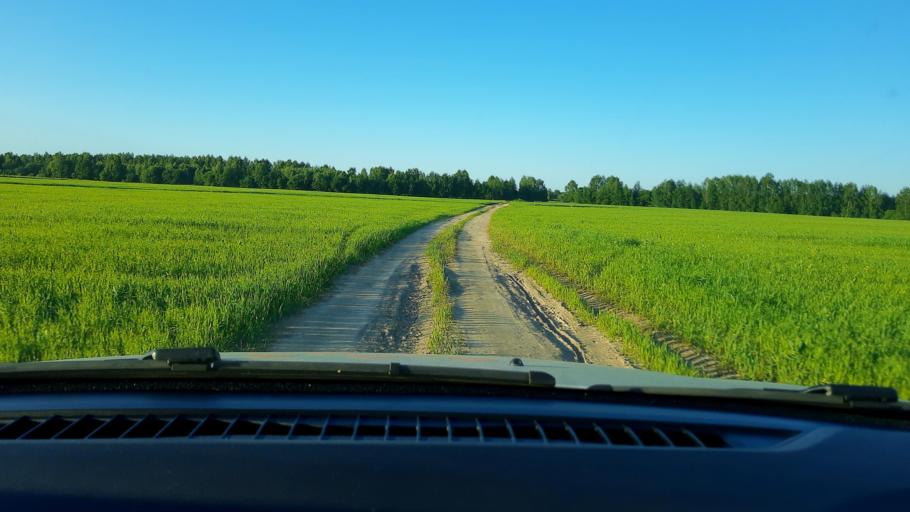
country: RU
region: Nizjnij Novgorod
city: Kstovo
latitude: 56.3040
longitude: 44.2603
